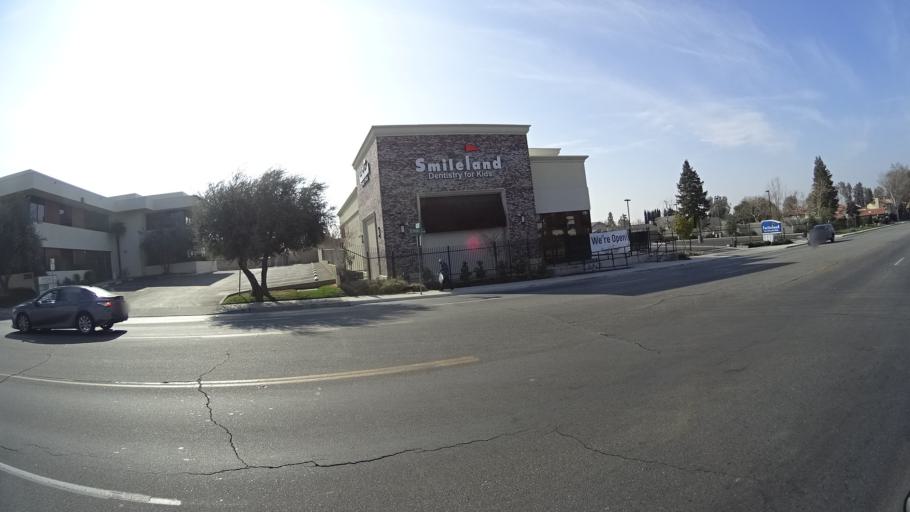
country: US
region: California
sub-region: Kern County
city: Bakersfield
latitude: 35.3924
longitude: -118.9509
